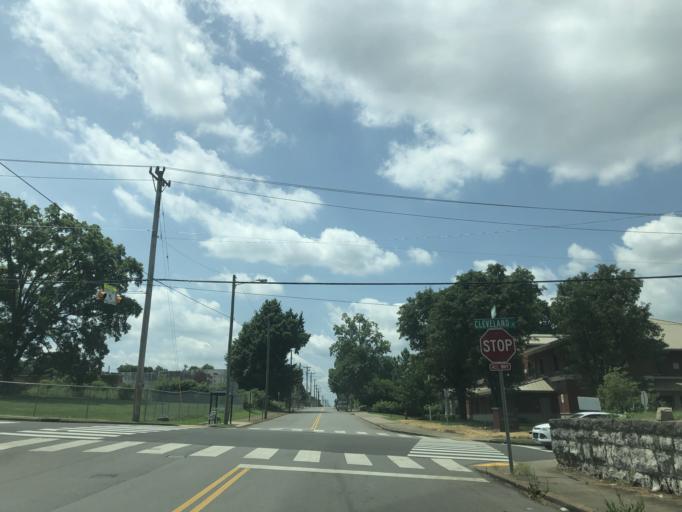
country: US
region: Tennessee
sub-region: Davidson County
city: Nashville
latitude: 36.1872
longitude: -86.7680
